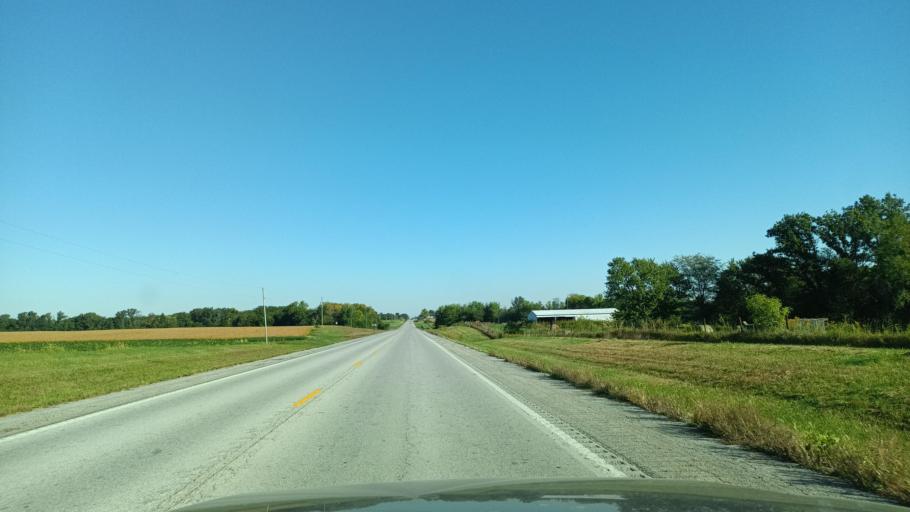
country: US
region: Missouri
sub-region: Audrain County
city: Vandalia
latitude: 39.2989
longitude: -91.6438
